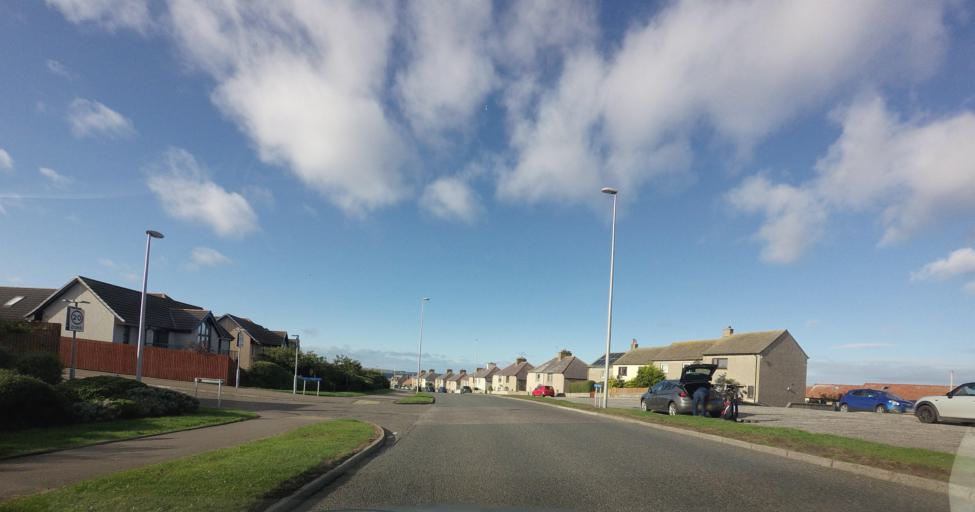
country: GB
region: Scotland
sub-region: Aberdeenshire
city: Macduff
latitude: 57.6698
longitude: -2.4812
